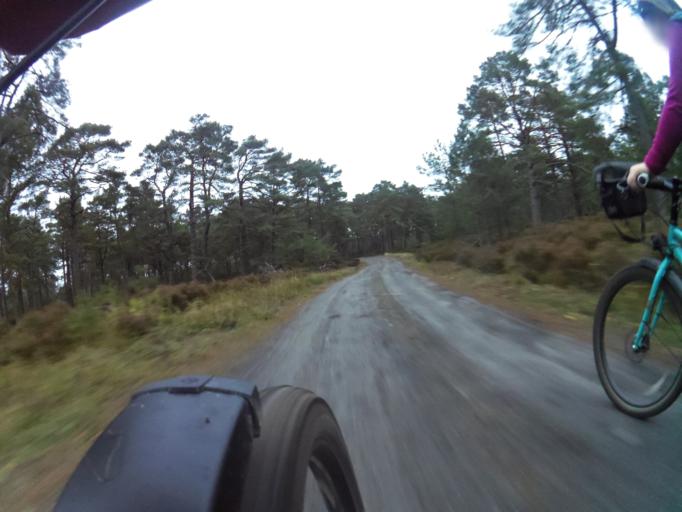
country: PL
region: Pomeranian Voivodeship
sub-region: Powiat wejherowski
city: Choczewo
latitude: 54.7990
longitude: 17.7799
